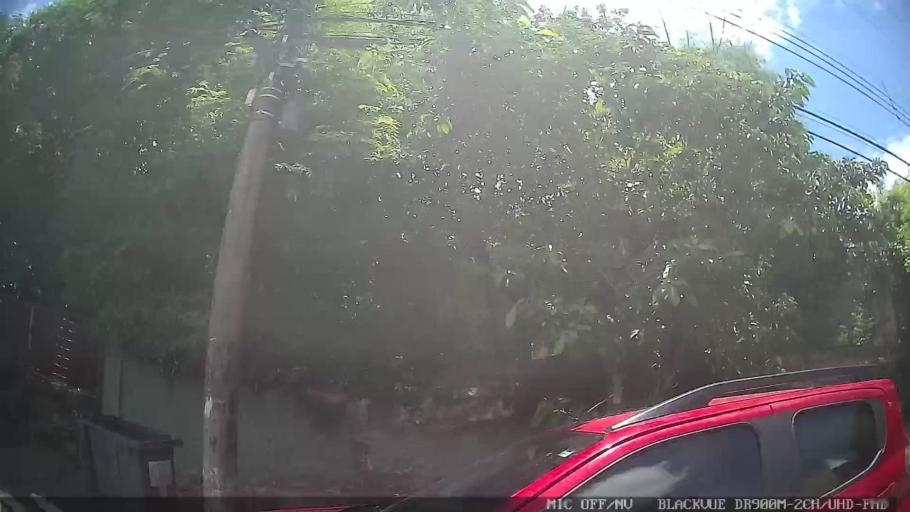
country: BR
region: Sao Paulo
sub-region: Laranjal Paulista
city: Laranjal Paulista
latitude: -23.0365
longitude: -47.8353
